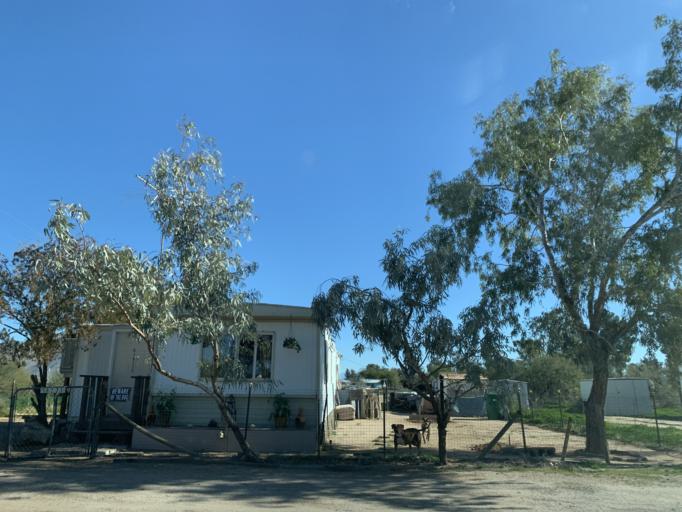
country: US
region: Arizona
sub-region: Pinal County
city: Eloy
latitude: 32.7140
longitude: -111.5030
